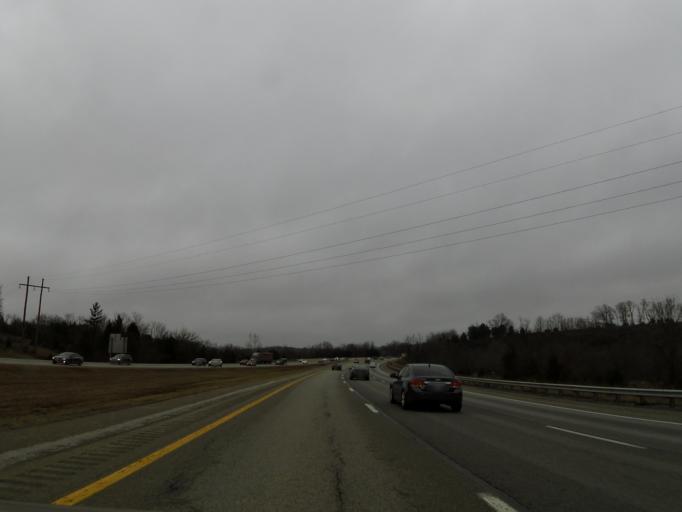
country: US
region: Kentucky
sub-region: Scott County
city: Georgetown
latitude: 38.3631
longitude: -84.5679
